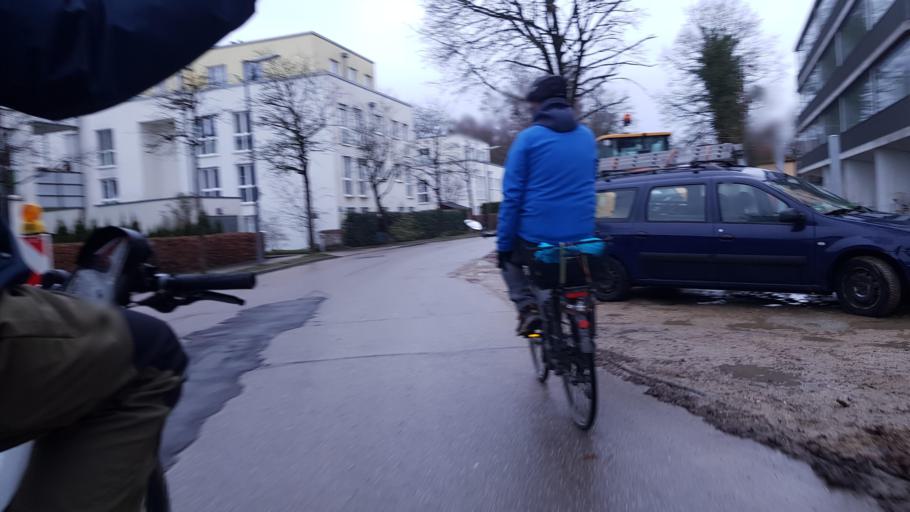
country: DE
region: Bavaria
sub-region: Upper Bavaria
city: Grobenzell
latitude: 48.1766
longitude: 11.4049
